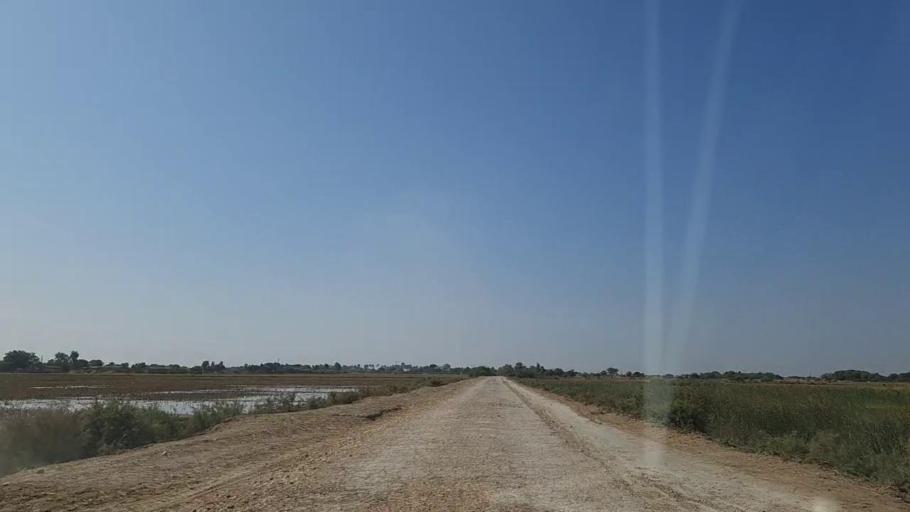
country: PK
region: Sindh
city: Chuhar Jamali
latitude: 24.4244
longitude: 68.0084
